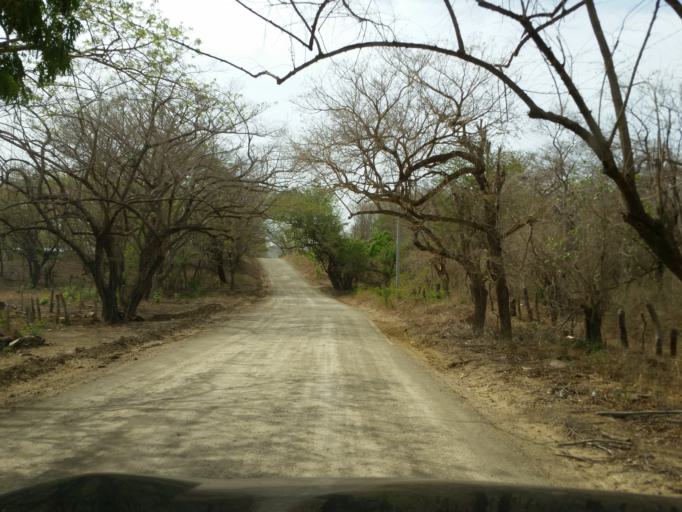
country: NI
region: Rivas
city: Tola
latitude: 11.4414
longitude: -86.0424
